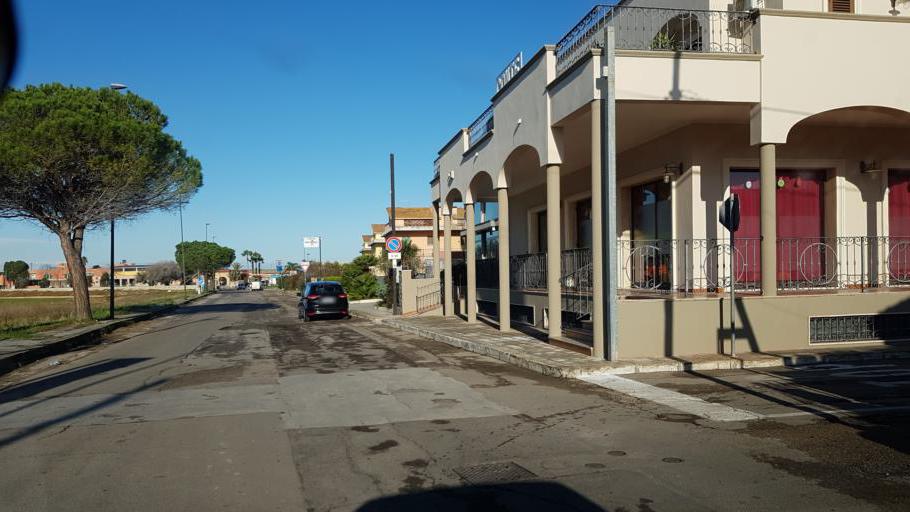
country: IT
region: Apulia
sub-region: Provincia di Brindisi
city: Torchiarolo
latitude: 40.4852
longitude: 18.0471
